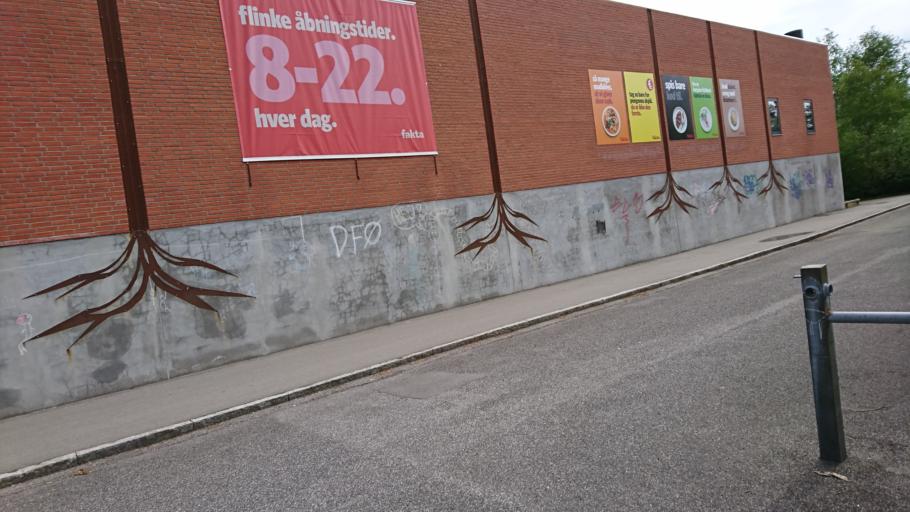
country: DK
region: Capital Region
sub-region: Ballerup Kommune
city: Malov
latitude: 55.7503
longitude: 12.3355
